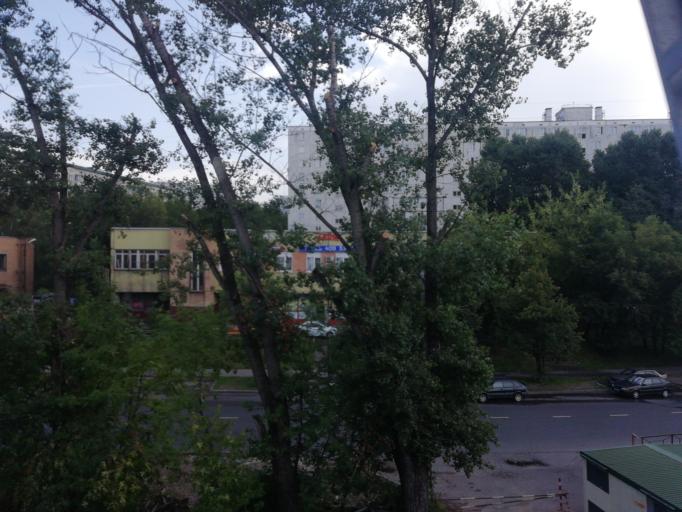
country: RU
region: Moskovskaya
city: Marfino
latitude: 55.7200
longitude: 37.3872
